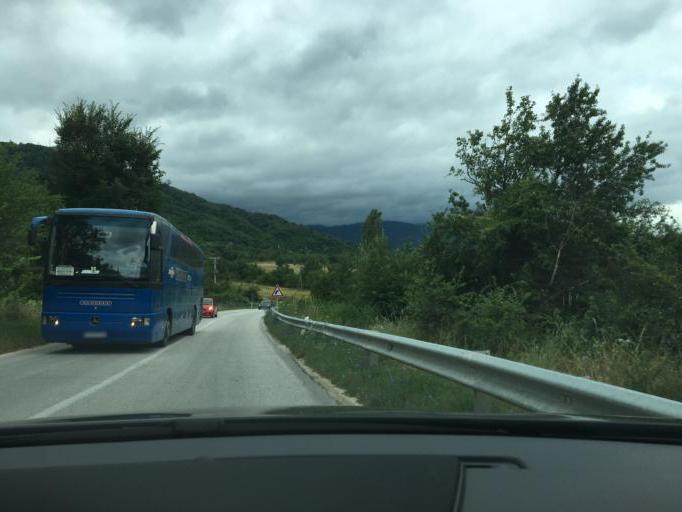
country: MK
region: Kriva Palanka
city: Kriva Palanka
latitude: 42.1805
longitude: 22.2725
